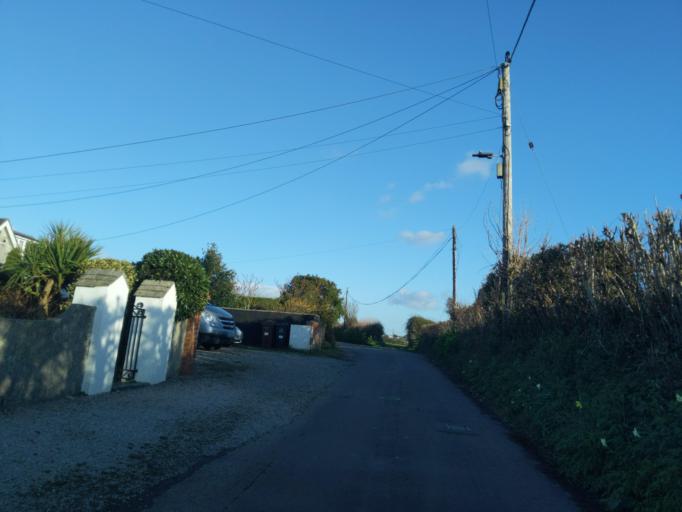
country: GB
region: England
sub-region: Devon
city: Wembury
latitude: 50.3351
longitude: -4.0717
